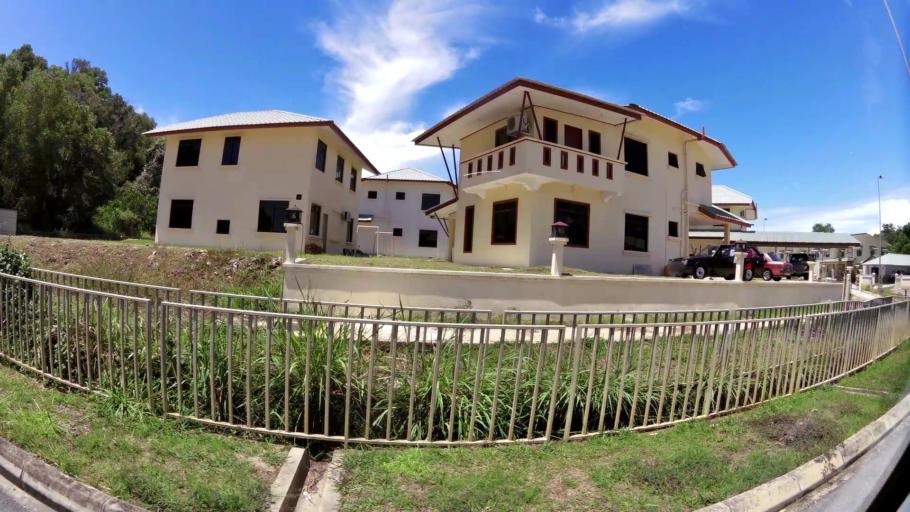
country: BN
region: Brunei and Muara
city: Bandar Seri Begawan
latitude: 5.0293
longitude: 115.0374
